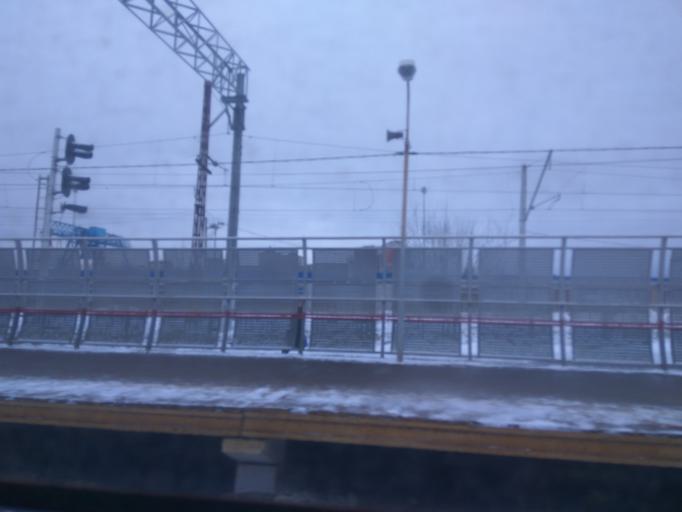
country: RU
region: Moskovskaya
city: Shcherbinka
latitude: 55.4707
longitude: 37.5555
